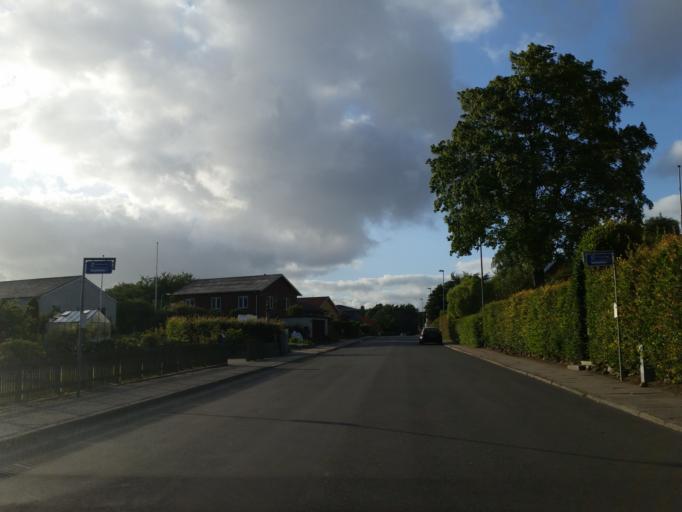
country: DK
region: South Denmark
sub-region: Vejle Kommune
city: Brejning
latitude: 55.6634
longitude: 9.6733
